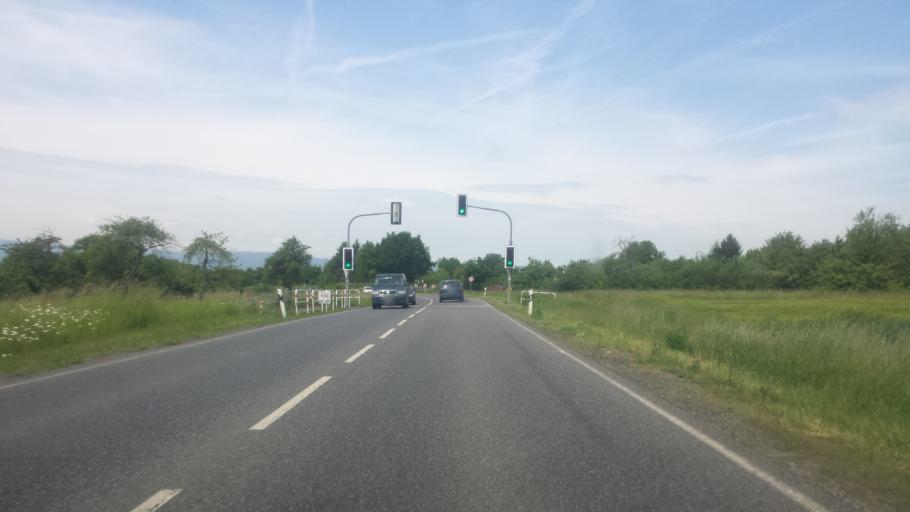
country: DE
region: Hesse
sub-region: Regierungsbezirk Darmstadt
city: Bad Vilbel
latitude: 50.1957
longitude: 8.7209
